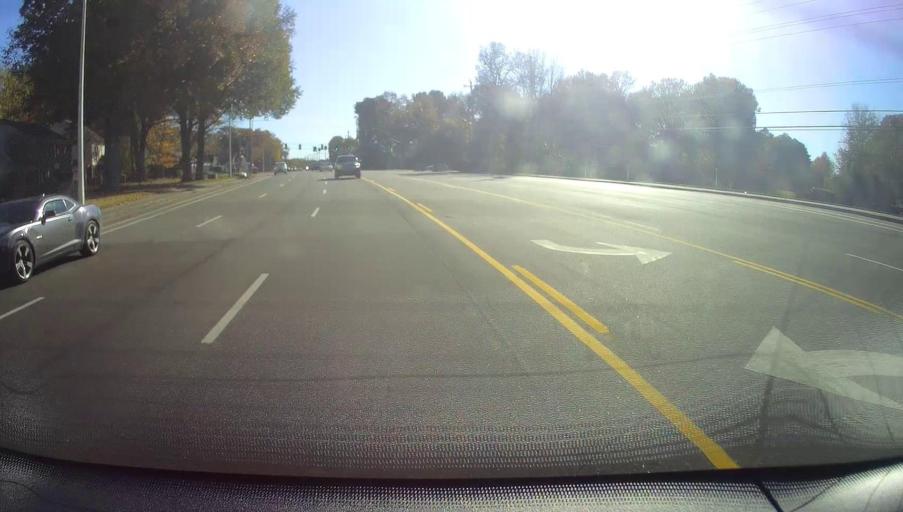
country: US
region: Tennessee
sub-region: Shelby County
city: Germantown
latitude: 35.0783
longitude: -89.8418
